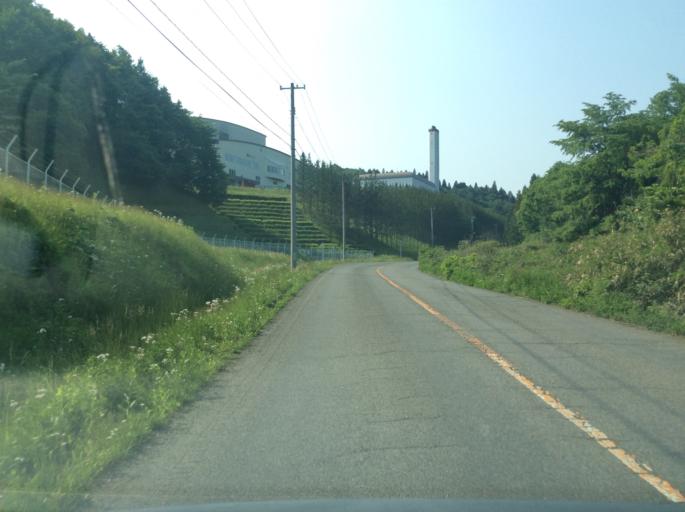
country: JP
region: Tochigi
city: Kuroiso
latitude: 37.0833
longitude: 140.2245
